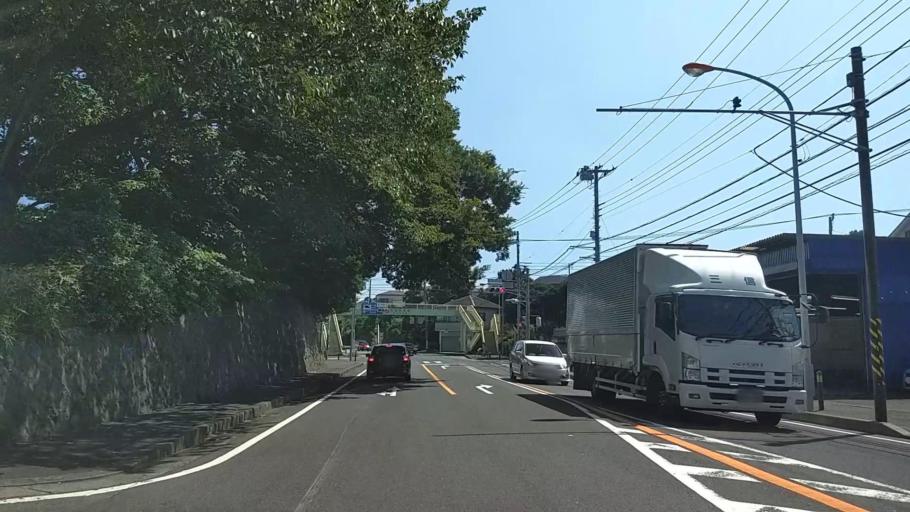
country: JP
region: Kanagawa
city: Fujisawa
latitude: 35.3531
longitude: 139.4911
